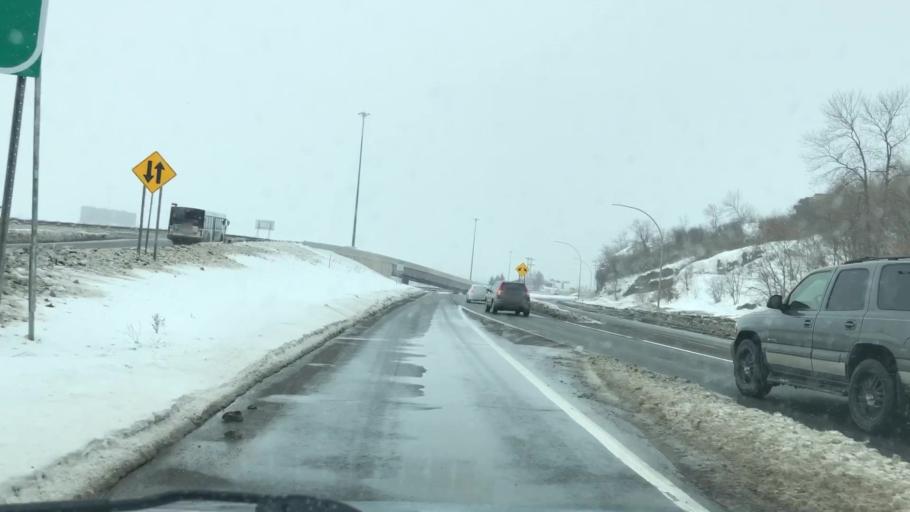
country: US
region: Minnesota
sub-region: Saint Louis County
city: Duluth
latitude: 46.7780
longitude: -92.1089
